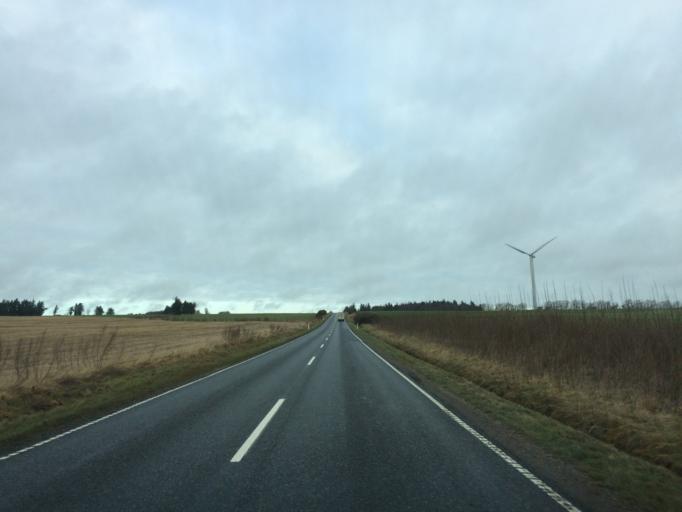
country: DK
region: Central Jutland
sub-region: Struer Kommune
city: Struer
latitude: 56.4222
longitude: 8.5025
